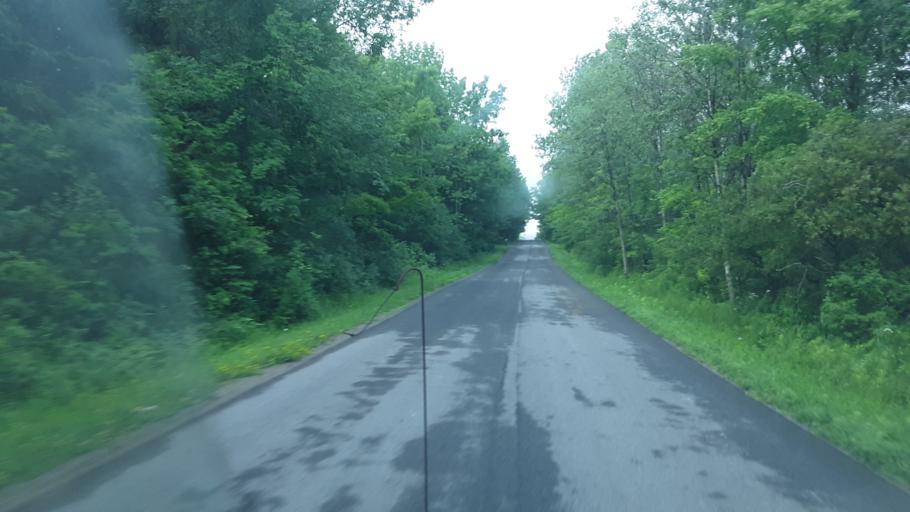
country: US
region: New York
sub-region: Montgomery County
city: Fonda
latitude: 42.8664
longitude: -74.3618
